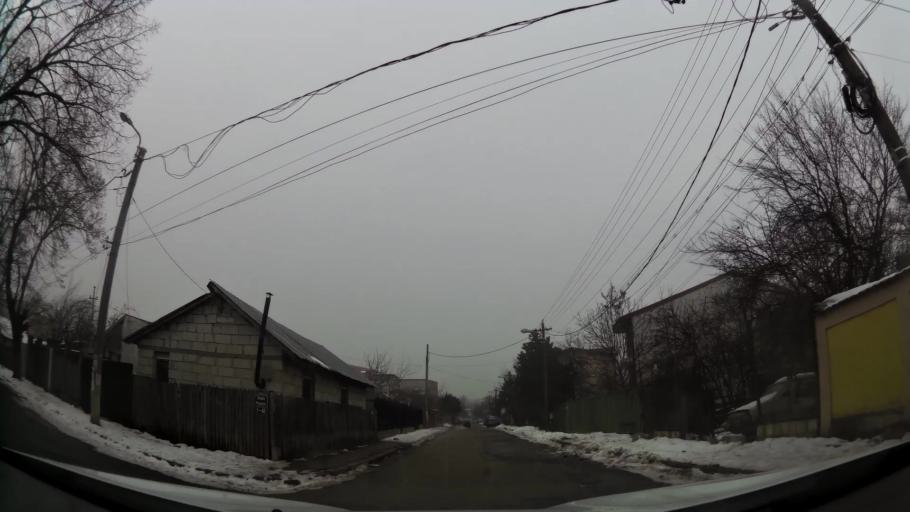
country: RO
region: Ilfov
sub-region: Comuna Chiajna
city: Rosu
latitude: 44.4463
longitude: 26.0248
